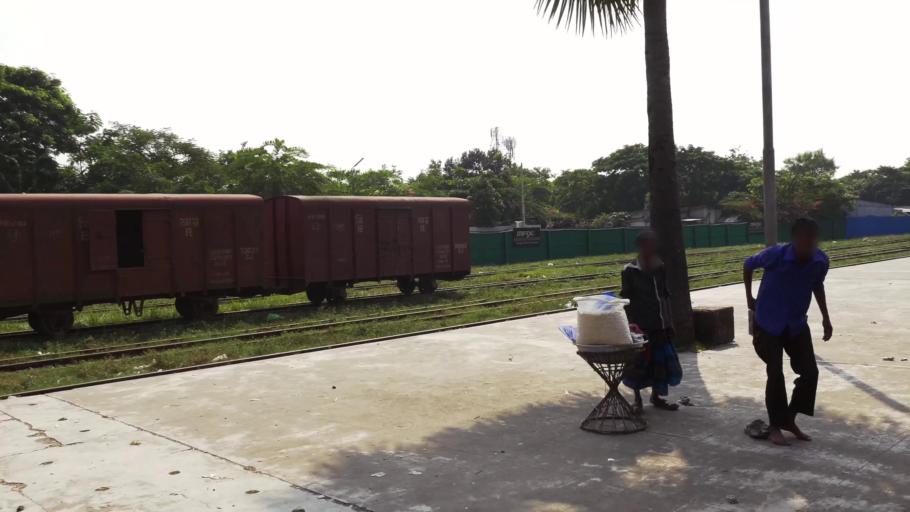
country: BD
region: Dhaka
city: Tungi
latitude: 23.8642
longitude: 90.4061
